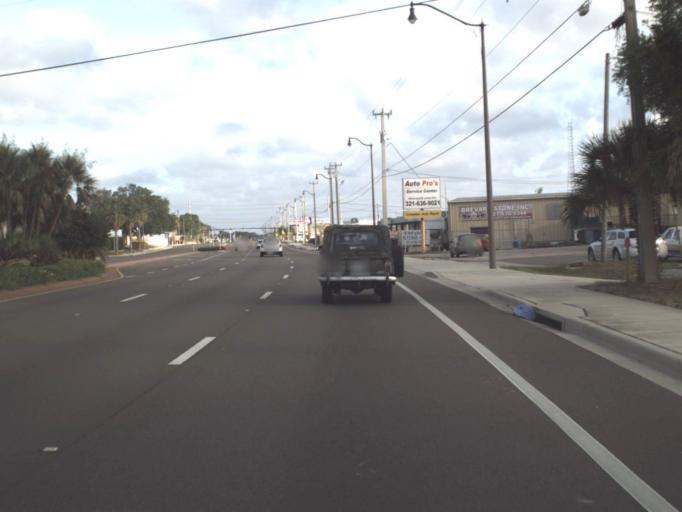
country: US
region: Florida
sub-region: Brevard County
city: Rockledge
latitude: 28.3546
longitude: -80.7325
